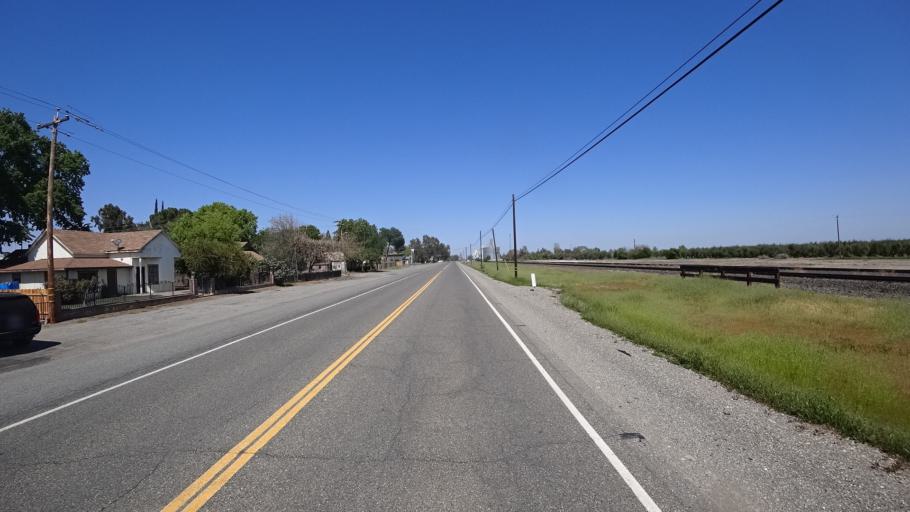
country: US
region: California
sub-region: Glenn County
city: Willows
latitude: 39.6169
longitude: -122.1941
